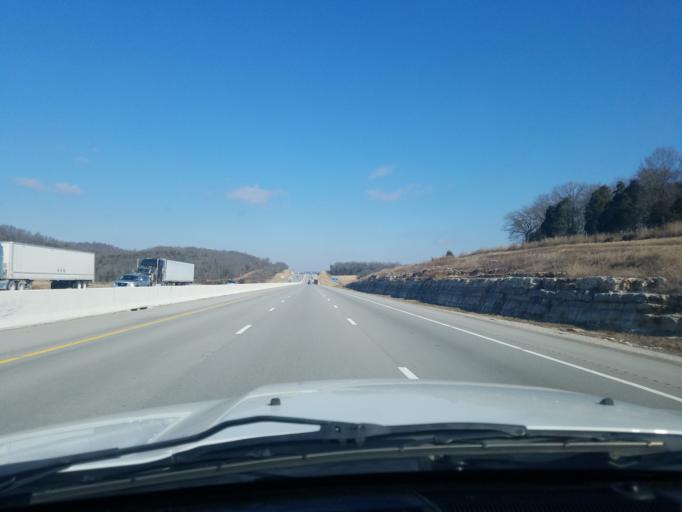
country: US
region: Kentucky
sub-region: Hart County
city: Horse Cave
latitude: 37.2170
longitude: -85.9348
